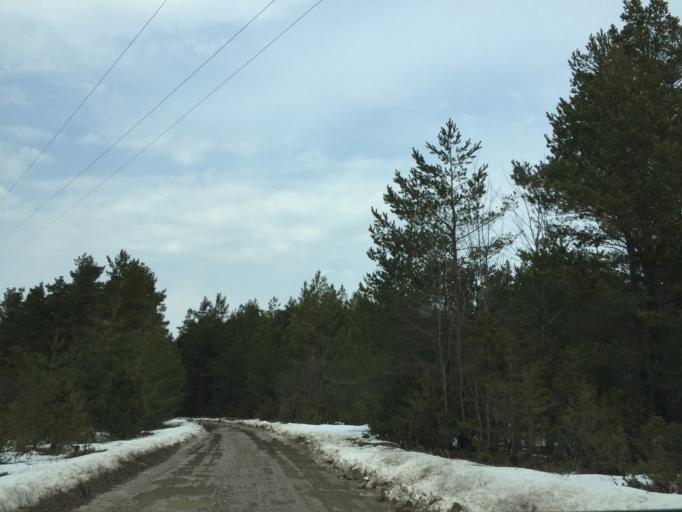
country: EE
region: Saare
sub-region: Kuressaare linn
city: Kuressaare
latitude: 58.4296
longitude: 22.1445
